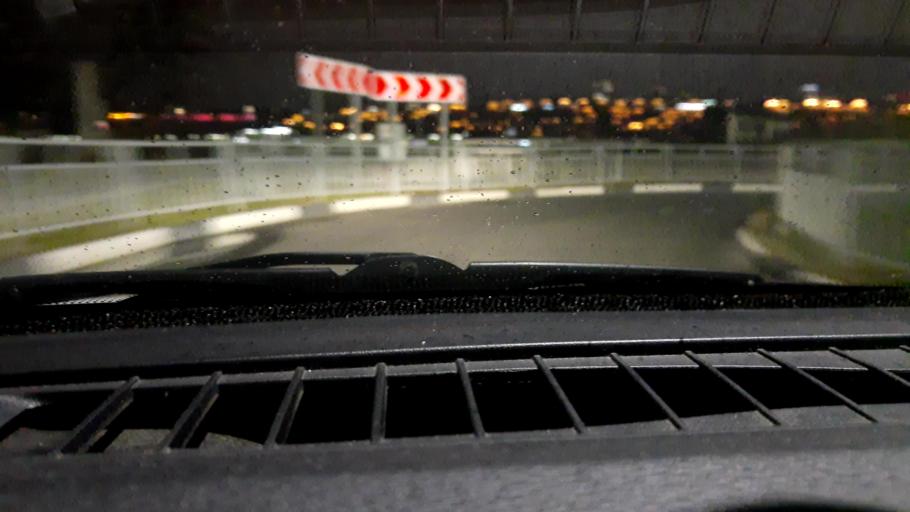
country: RU
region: Nizjnij Novgorod
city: Nizhniy Novgorod
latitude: 56.3346
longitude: 43.9734
